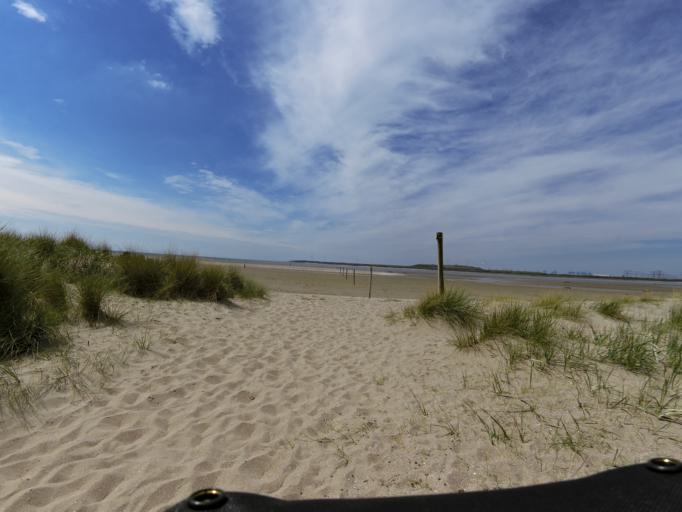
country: NL
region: South Holland
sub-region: Gemeente Hellevoetsluis
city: Nieuw-Helvoet
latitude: 51.9103
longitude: 4.0511
